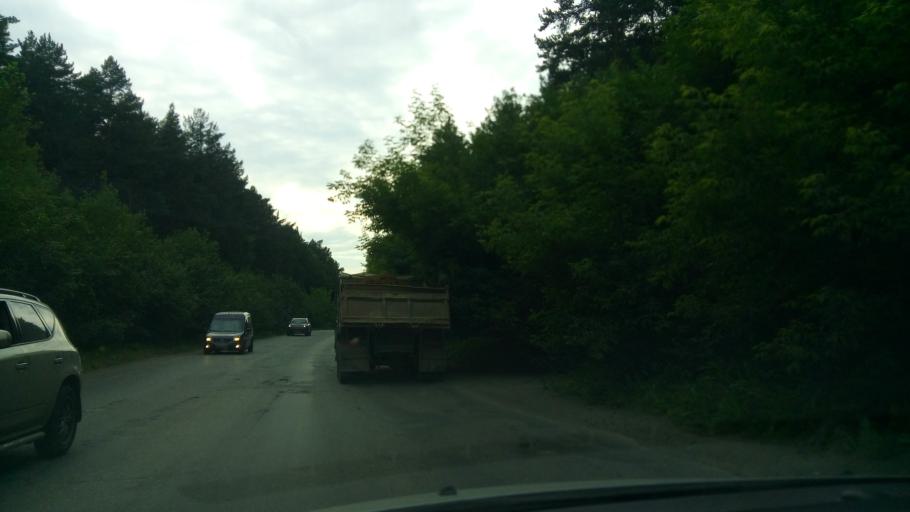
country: RU
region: Sverdlovsk
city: Yekaterinburg
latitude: 56.8864
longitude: 60.6766
